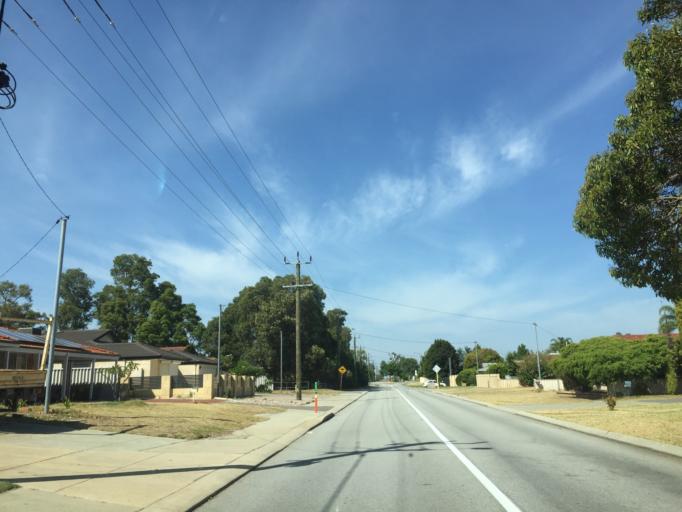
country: AU
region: Western Australia
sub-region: Gosnells
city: Thornlie
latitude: -32.0801
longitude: 115.9627
